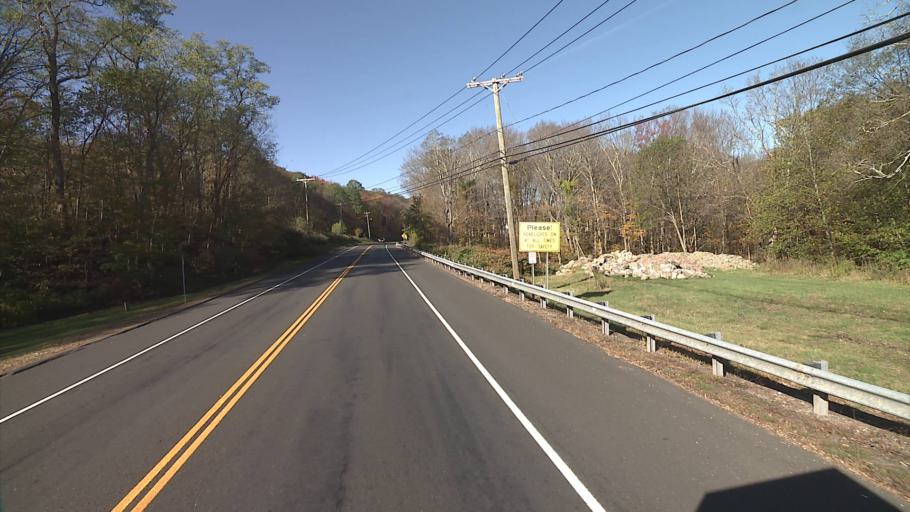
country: US
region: Connecticut
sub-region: Tolland County
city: Coventry Lake
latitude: 41.7387
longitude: -72.3712
